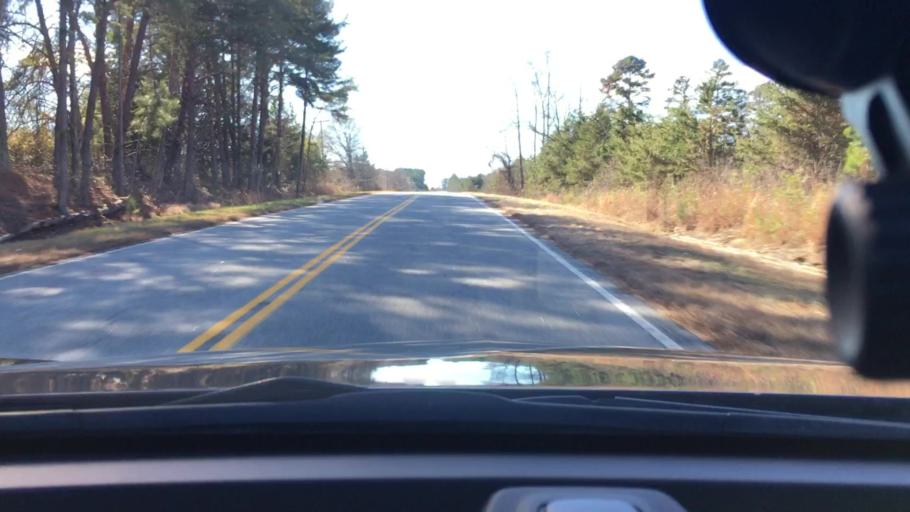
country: US
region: South Carolina
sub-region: Spartanburg County
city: Pacolet
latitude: 34.9626
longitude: -81.7073
